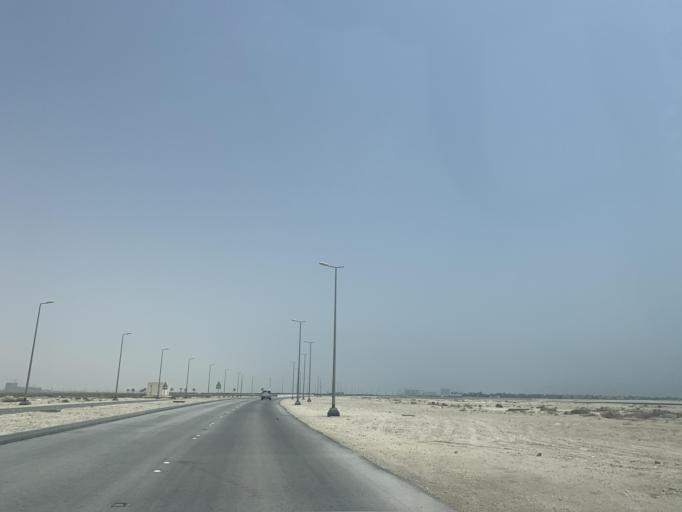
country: BH
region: Central Governorate
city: Dar Kulayb
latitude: 25.8395
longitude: 50.5923
